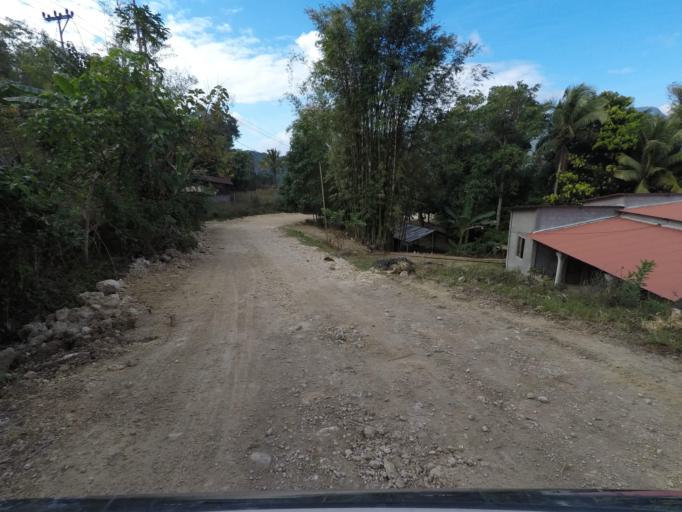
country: TL
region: Baucau
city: Venilale
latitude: -8.6448
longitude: 126.3911
